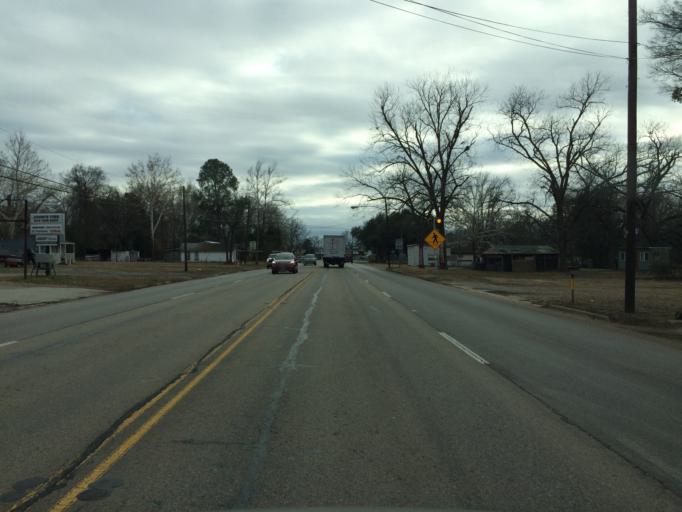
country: US
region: Texas
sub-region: Wood County
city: Mineola
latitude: 32.6586
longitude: -95.4897
